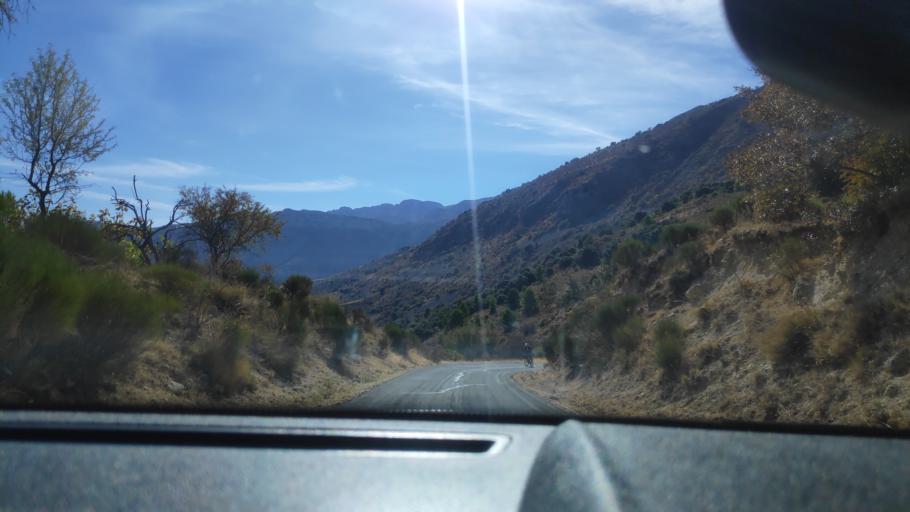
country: ES
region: Andalusia
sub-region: Provincia de Jaen
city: Torres
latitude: 37.7844
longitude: -3.4802
